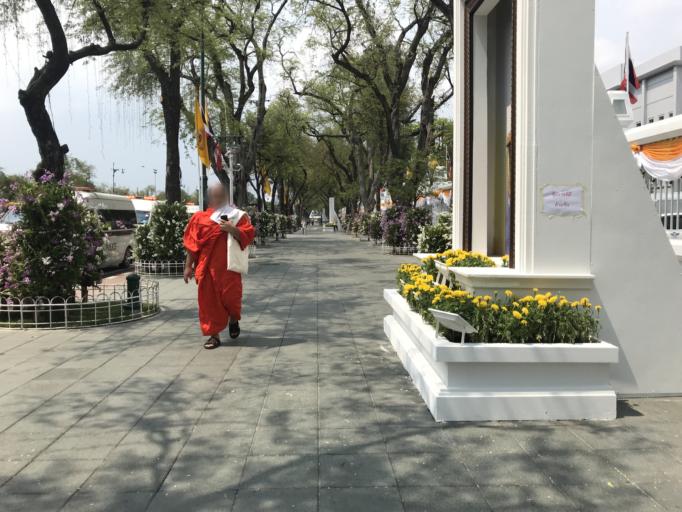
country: TH
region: Bangkok
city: Bangkok
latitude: 13.7546
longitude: 100.4942
